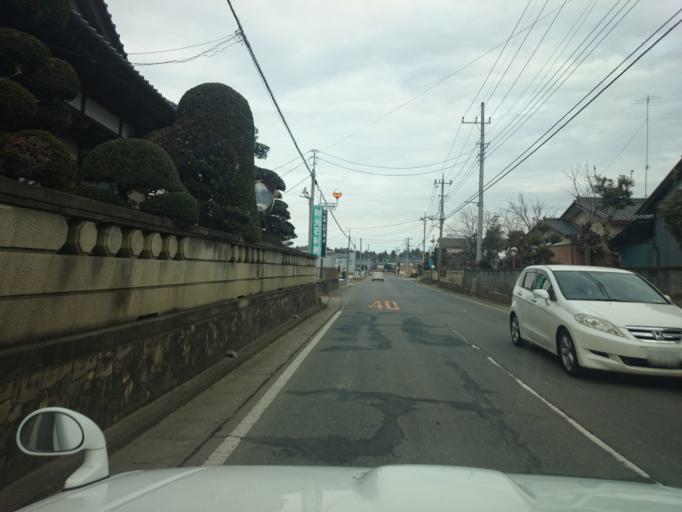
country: JP
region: Ibaraki
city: Ishige
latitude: 36.1085
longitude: 140.0479
